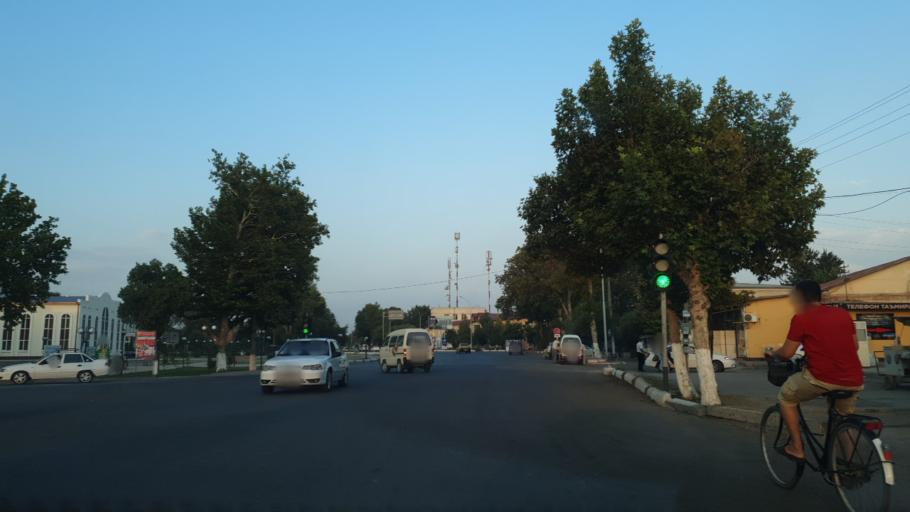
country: UZ
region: Fergana
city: Beshariq
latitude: 40.4368
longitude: 70.6053
